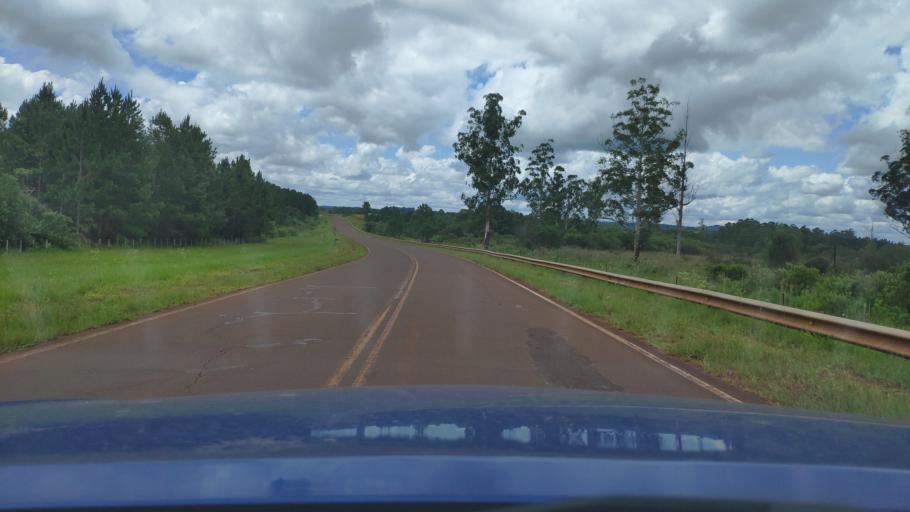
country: AR
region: Misiones
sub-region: Departamento de San Javier
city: San Javier
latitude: -27.8516
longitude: -55.2468
